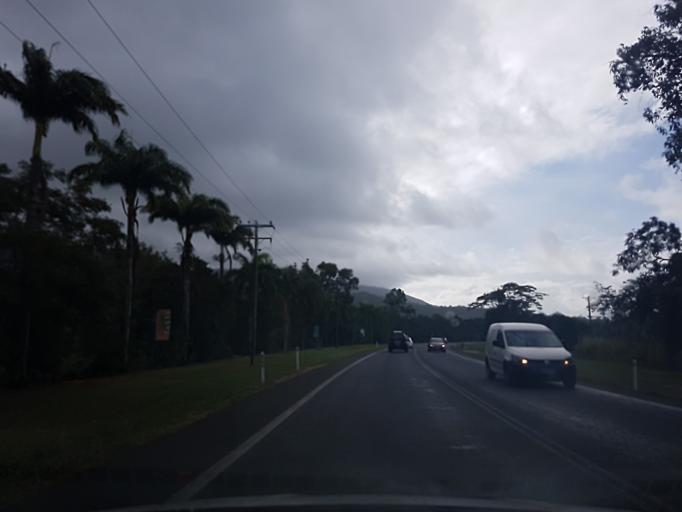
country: AU
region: Queensland
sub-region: Cairns
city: Trinity Beach
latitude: -16.7860
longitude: 145.6741
